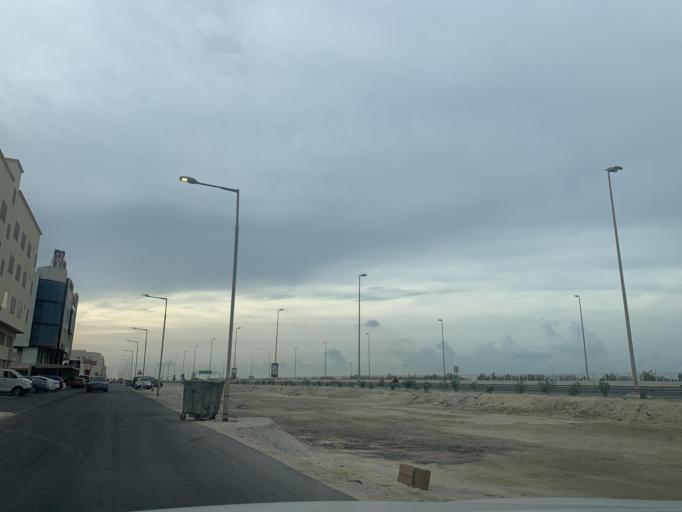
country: BH
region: Muharraq
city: Al Hadd
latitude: 26.2798
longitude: 50.6522
